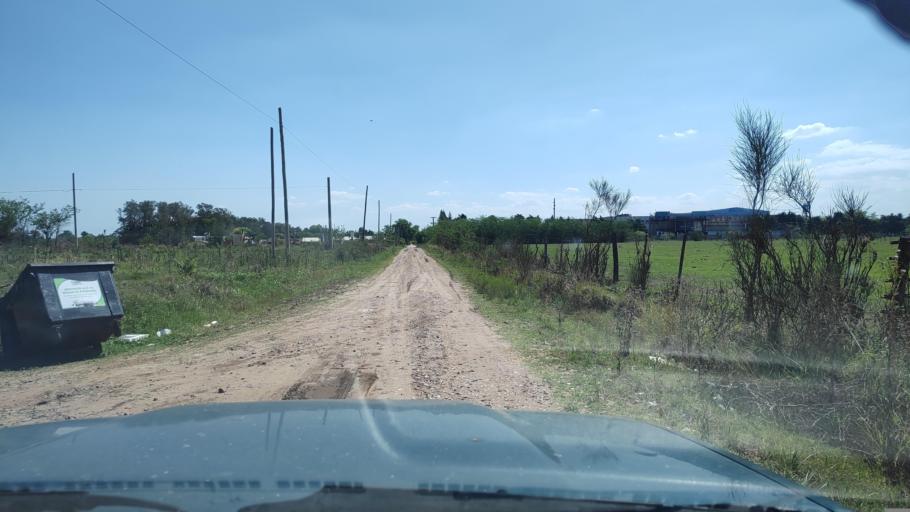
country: AR
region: Buenos Aires
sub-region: Partido de Lujan
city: Lujan
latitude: -34.5654
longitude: -59.1381
